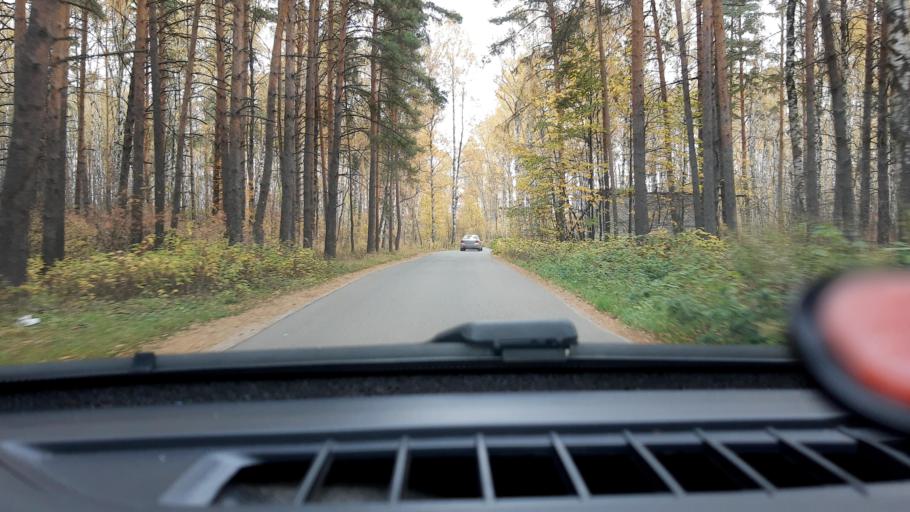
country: RU
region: Nizjnij Novgorod
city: Gorbatovka
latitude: 56.2894
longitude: 43.8273
